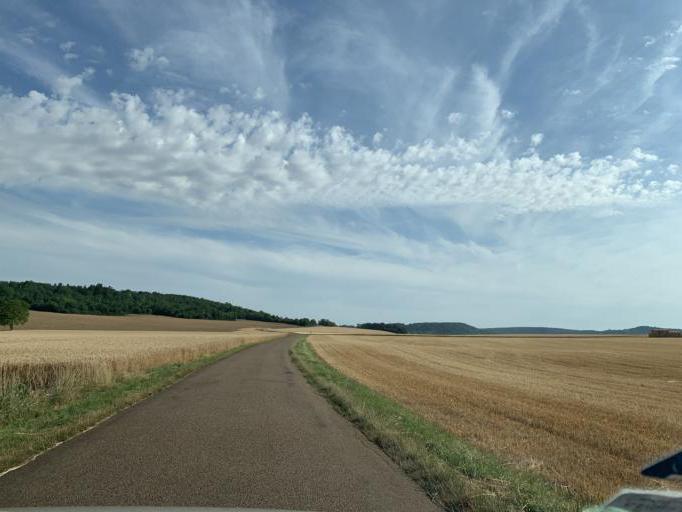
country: FR
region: Bourgogne
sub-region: Departement de la Nievre
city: Clamecy
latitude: 47.4585
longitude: 3.4248
